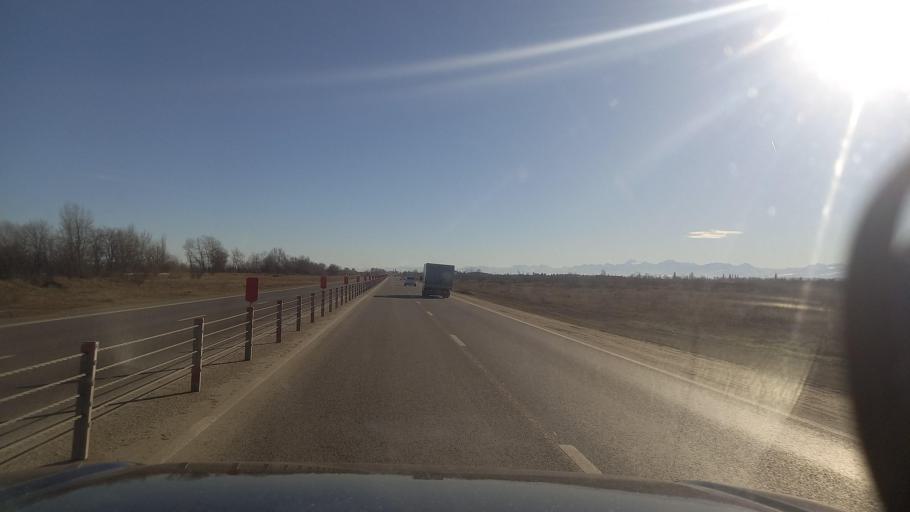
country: RU
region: Kabardino-Balkariya
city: Staryy Cherek
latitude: 43.4811
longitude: 43.8156
